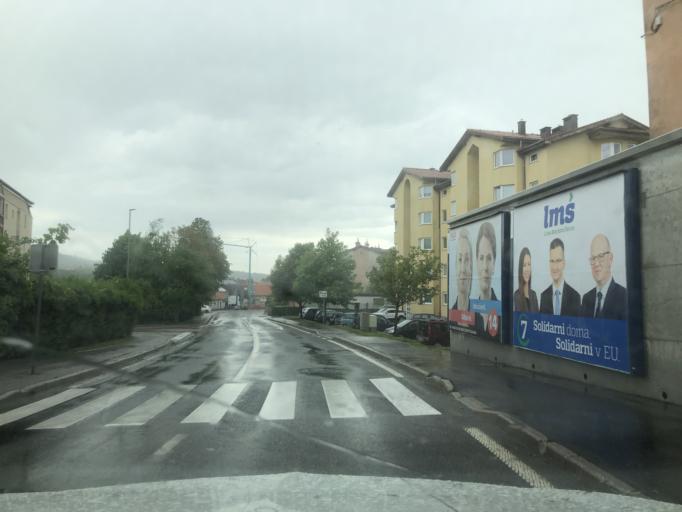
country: SI
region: Postojna
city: Postojna
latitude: 45.7812
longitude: 14.2164
